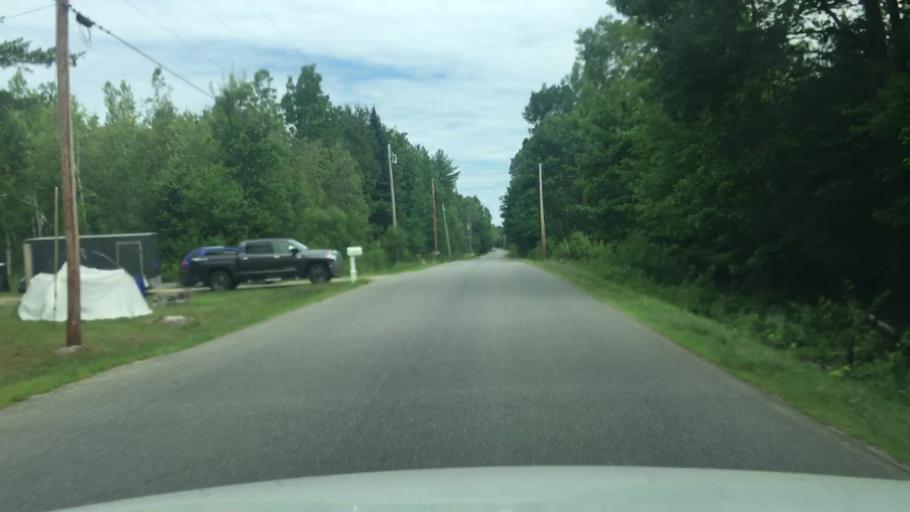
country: US
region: Maine
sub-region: Kennebec County
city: Clinton
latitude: 44.5961
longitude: -69.4717
